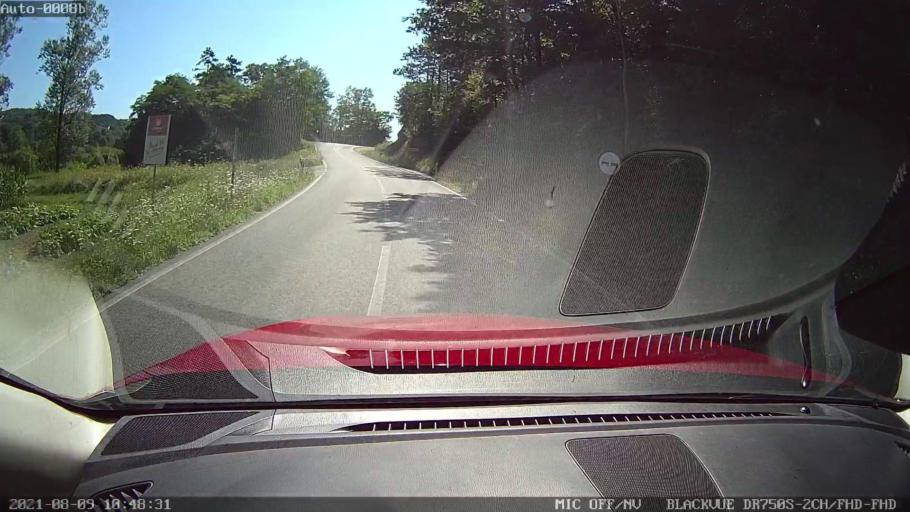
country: HR
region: Istarska
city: Pazin
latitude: 45.2709
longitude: 14.0244
